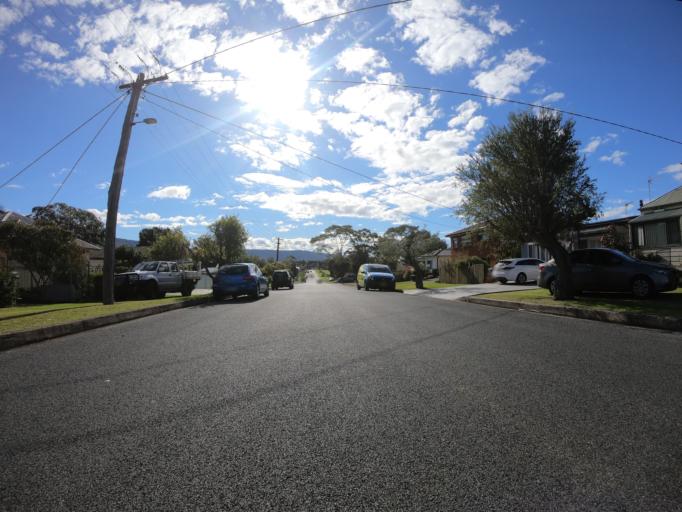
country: AU
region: New South Wales
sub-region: Wollongong
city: East Corrimal
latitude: -34.3666
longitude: 150.9118
